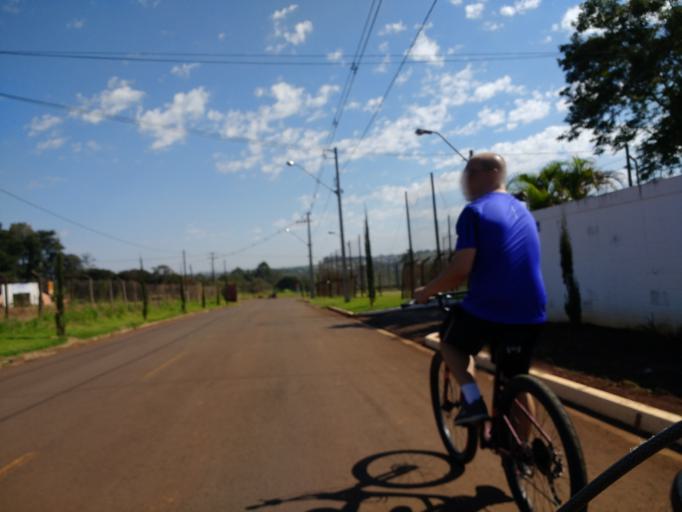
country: BR
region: Parana
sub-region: Londrina
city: Londrina
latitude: -23.3615
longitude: -51.1972
